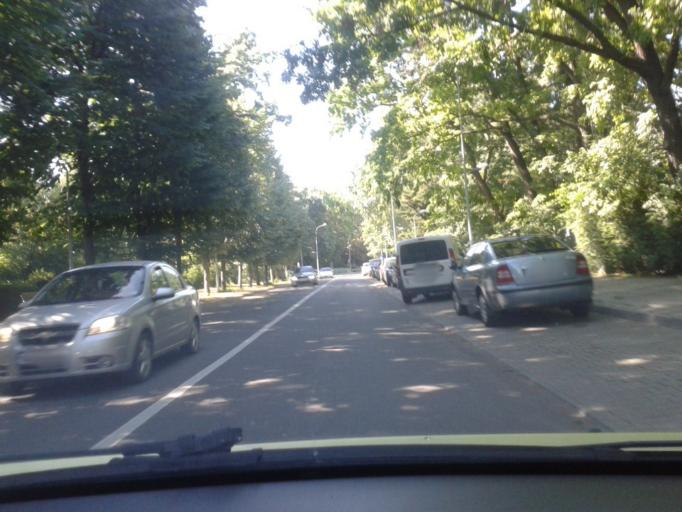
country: RO
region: Constanta
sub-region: Comuna Douazeci si Trei August
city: Douazeci si Trei August
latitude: 43.8766
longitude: 28.6030
